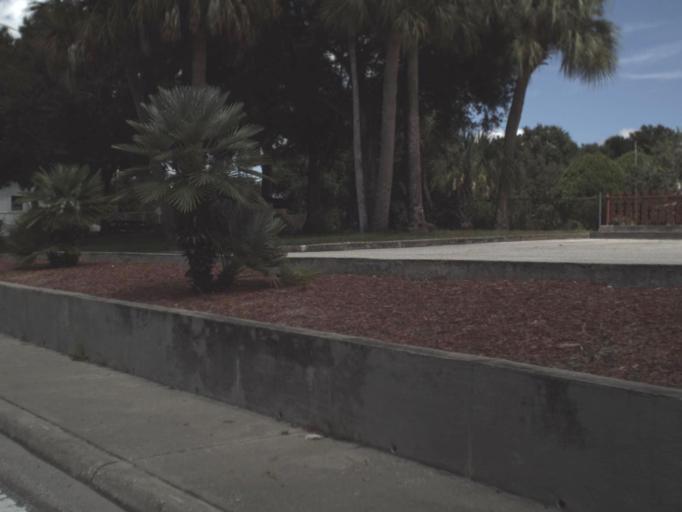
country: US
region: Florida
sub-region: Polk County
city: Lake Wales
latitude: 27.8983
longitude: -81.5848
